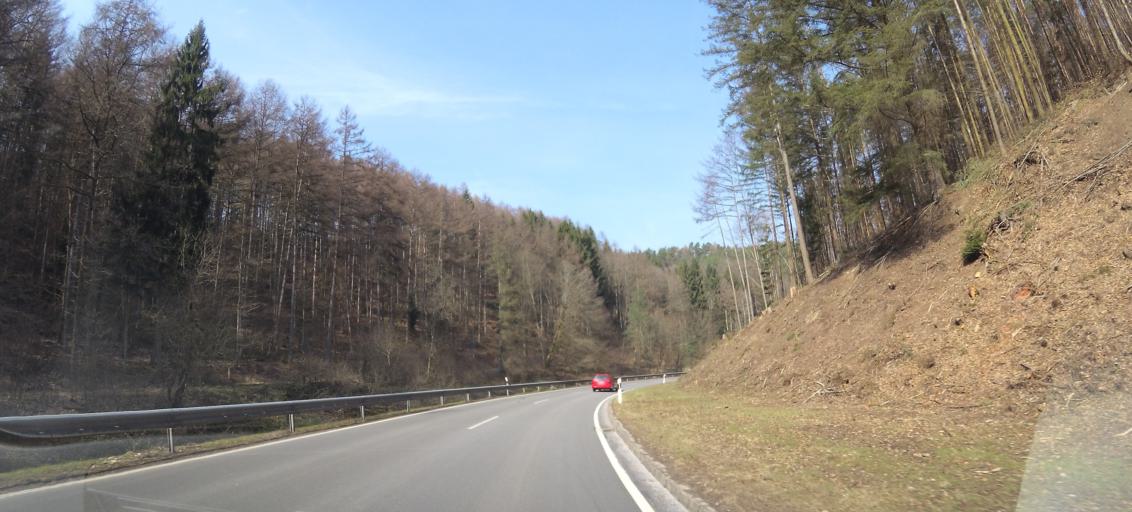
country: DE
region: Rheinland-Pfalz
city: Stelzenberg
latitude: 49.3836
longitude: 7.7388
